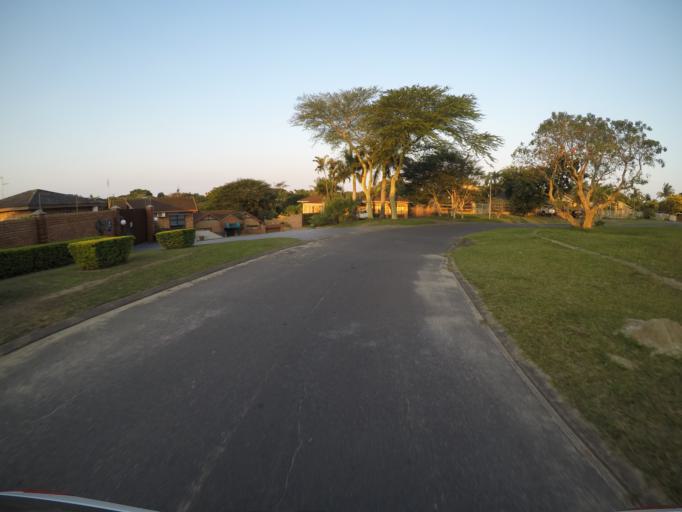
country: ZA
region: KwaZulu-Natal
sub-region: uThungulu District Municipality
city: Richards Bay
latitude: -28.7646
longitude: 32.1167
